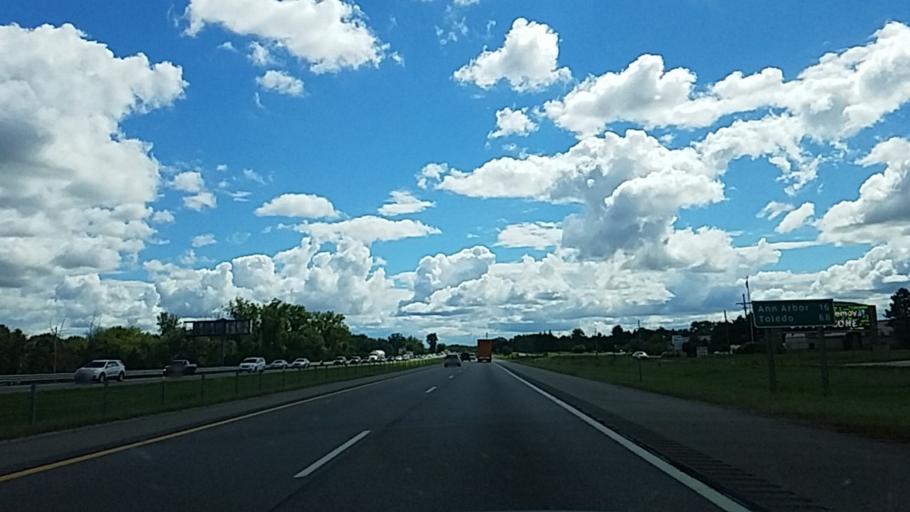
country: US
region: Michigan
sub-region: Livingston County
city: Brighton
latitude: 42.4937
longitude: -83.7577
